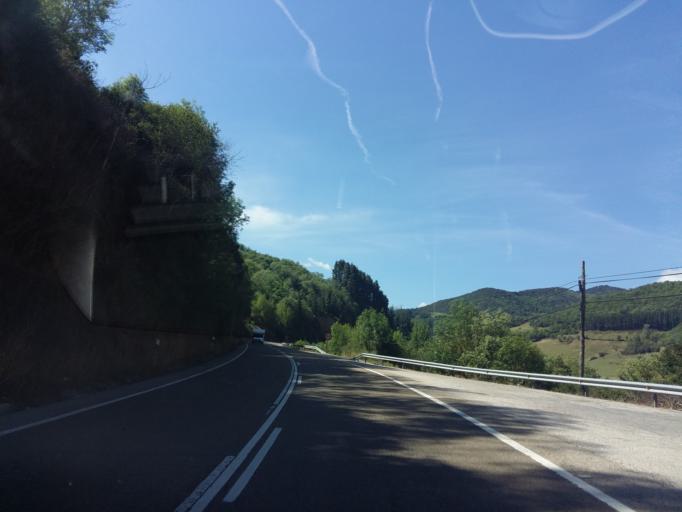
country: ES
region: Cantabria
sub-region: Provincia de Cantabria
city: Potes
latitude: 43.1936
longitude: -4.6036
